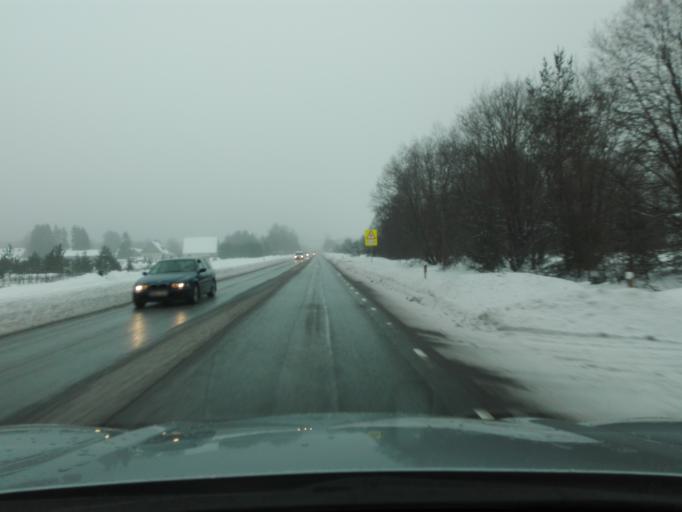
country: EE
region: Harju
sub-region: Kiili vald
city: Kiili
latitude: 59.3429
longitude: 24.7740
